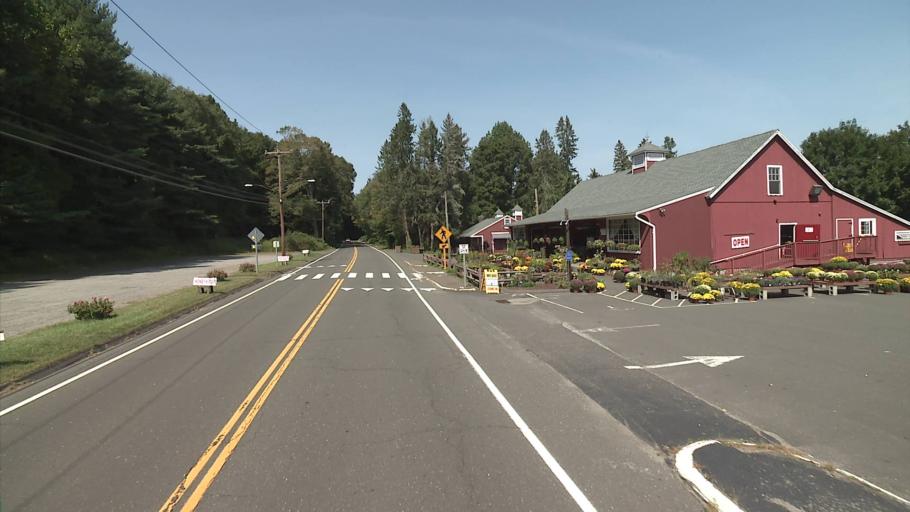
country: US
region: Connecticut
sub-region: Fairfield County
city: Georgetown
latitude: 41.2553
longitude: -73.3236
